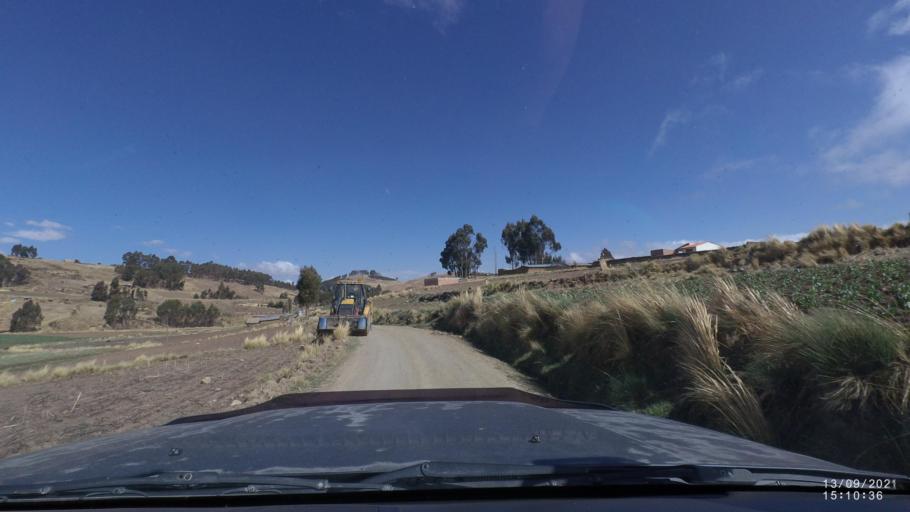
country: BO
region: Cochabamba
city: Colomi
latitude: -17.3556
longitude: -65.8047
